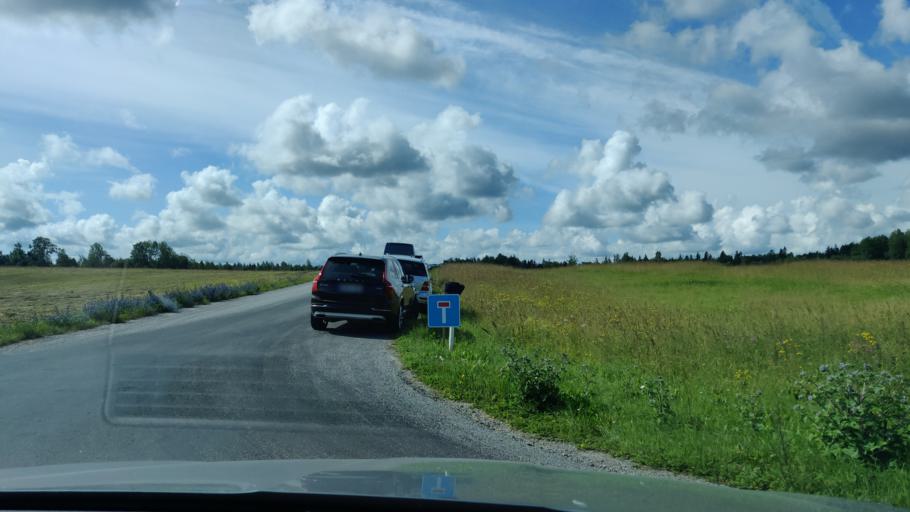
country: EE
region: Tartu
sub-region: Elva linn
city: Elva
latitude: 58.0384
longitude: 26.3544
